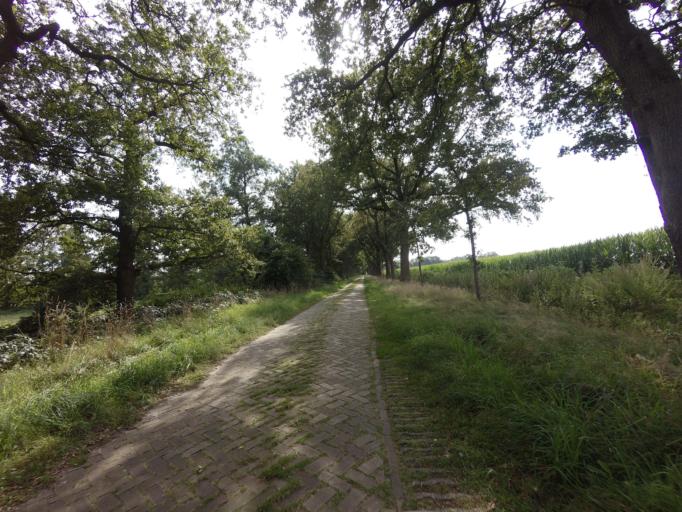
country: NL
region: Drenthe
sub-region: Gemeente Coevorden
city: Sleen
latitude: 52.7788
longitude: 6.7249
